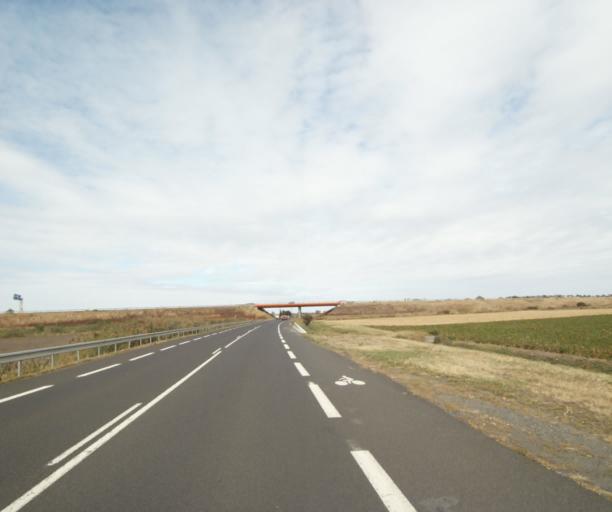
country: FR
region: Auvergne
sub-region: Departement du Puy-de-Dome
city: Malintrat
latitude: 45.7830
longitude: 3.2027
